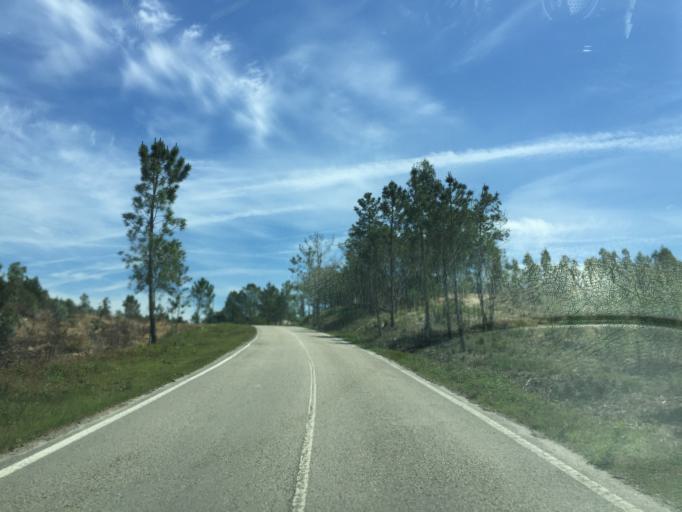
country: PT
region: Coimbra
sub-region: Soure
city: Soure
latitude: 40.0611
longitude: -8.6935
